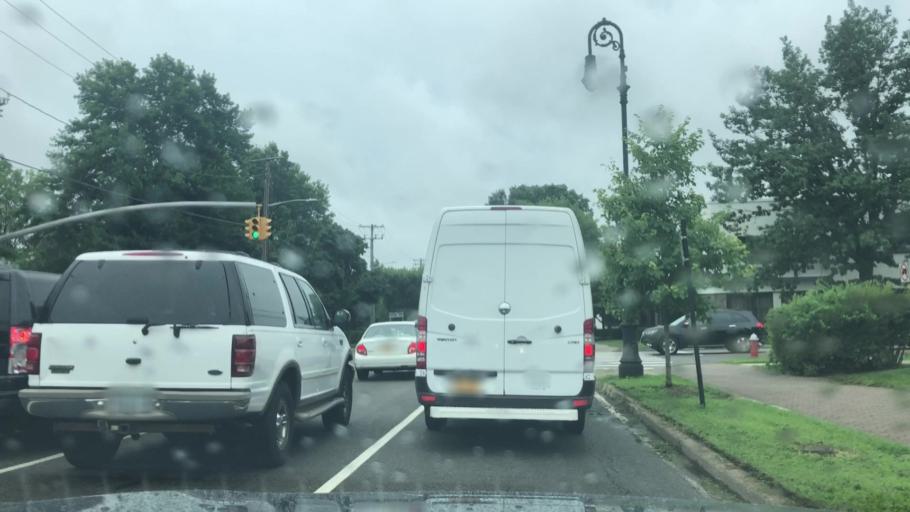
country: US
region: New York
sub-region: Nassau County
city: Garden City
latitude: 40.7239
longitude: -73.6335
